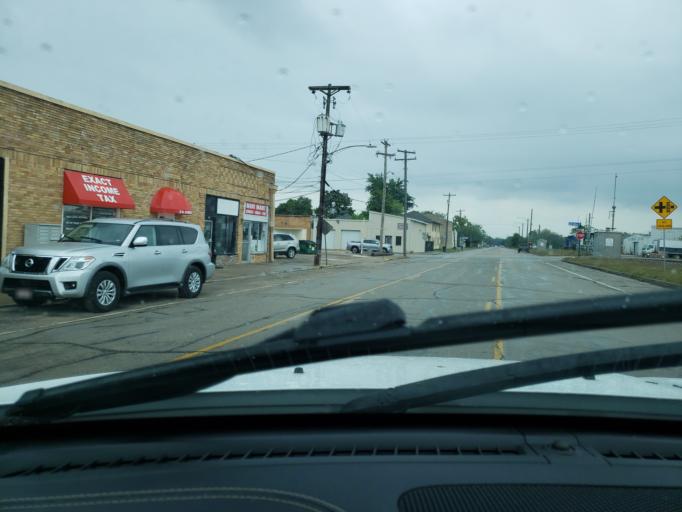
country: US
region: Texas
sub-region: Harris County
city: Baytown
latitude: 29.7324
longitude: -94.9685
